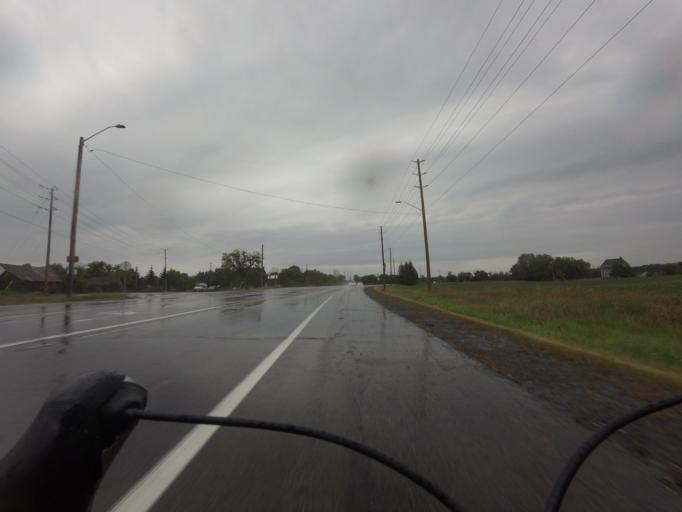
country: CA
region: Ontario
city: Bells Corners
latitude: 45.2230
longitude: -75.7180
